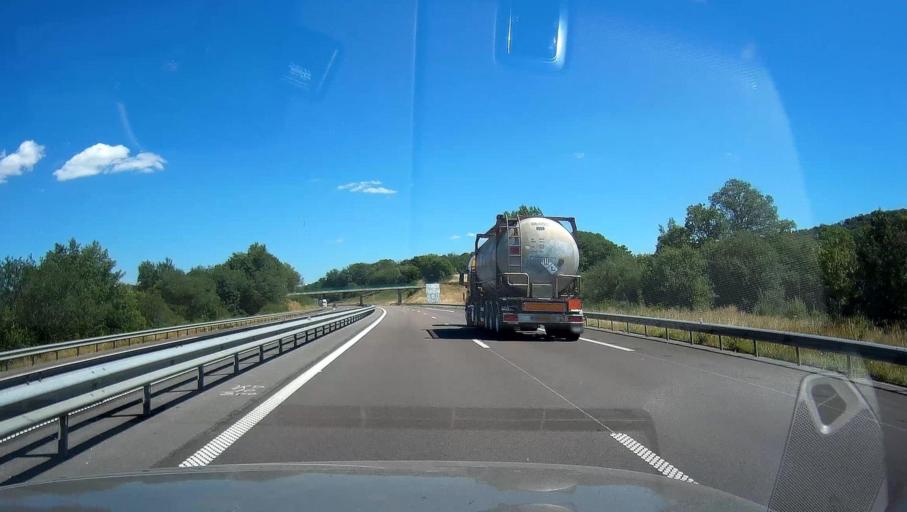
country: FR
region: Champagne-Ardenne
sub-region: Departement des Ardennes
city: La Francheville
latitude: 49.6398
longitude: 4.6151
